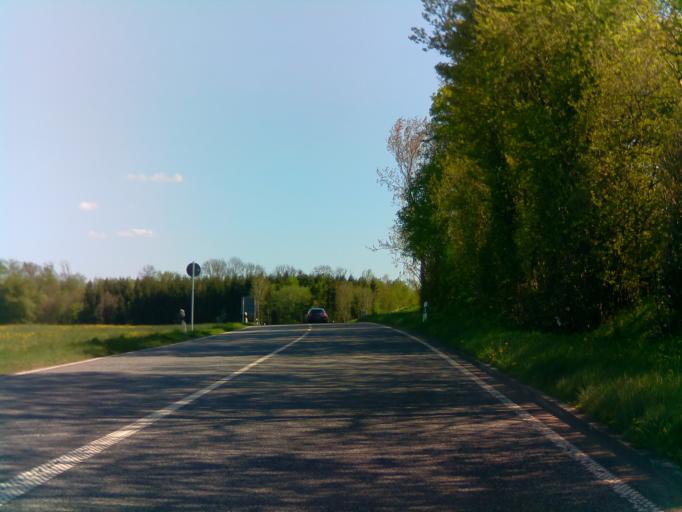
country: DE
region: Hesse
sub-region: Regierungsbezirk Giessen
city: Grebenhain
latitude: 50.4311
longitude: 9.3248
